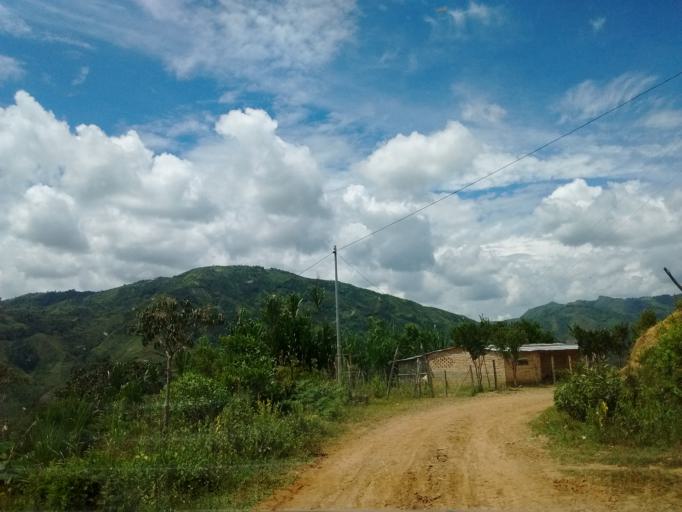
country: CO
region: Cauca
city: Villa Rica
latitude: 2.6628
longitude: -76.7658
